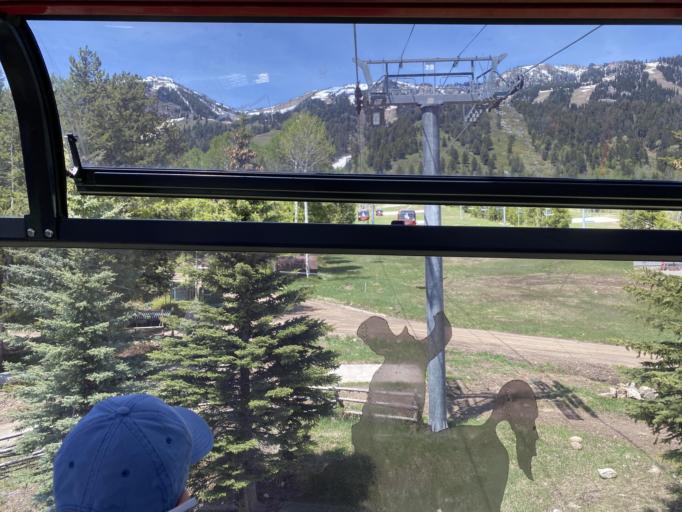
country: US
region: Wyoming
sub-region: Teton County
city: Moose Wilson Road
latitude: 43.5892
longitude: -110.8292
